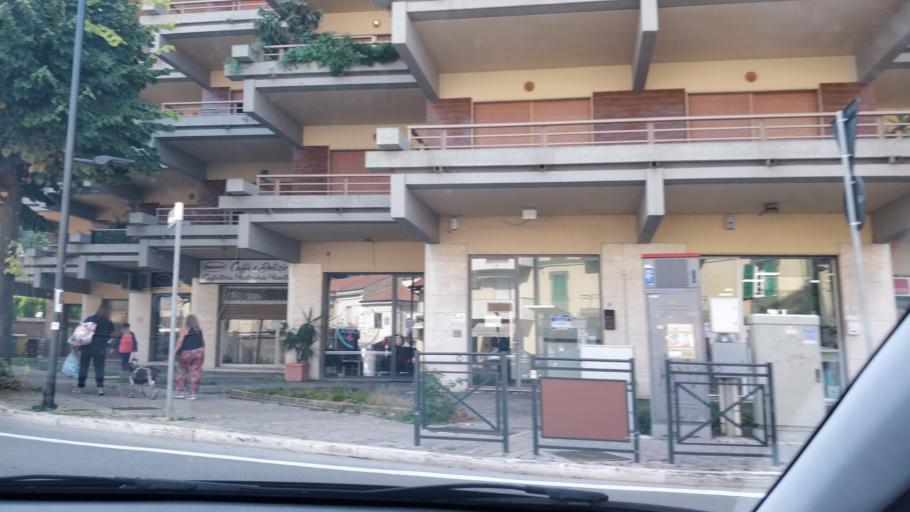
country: IT
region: Abruzzo
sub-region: Provincia di Chieti
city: Chieti
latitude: 42.3548
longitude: 14.1382
